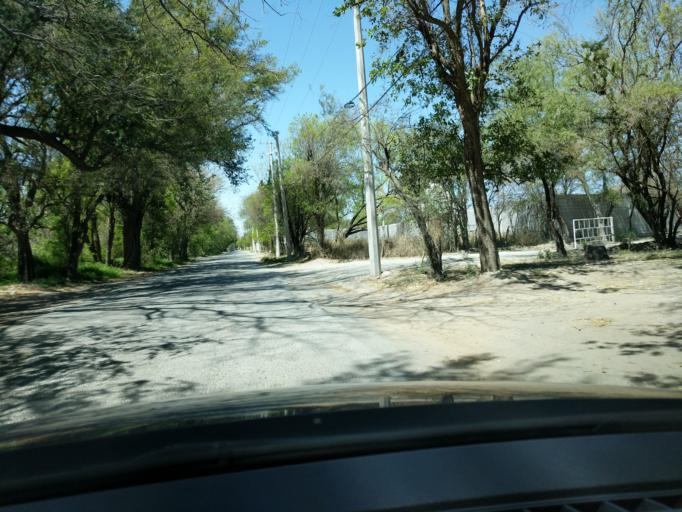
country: MX
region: Nuevo Leon
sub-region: Pesqueria
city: Colinas del Aeropuerto
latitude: 25.8118
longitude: -100.1270
